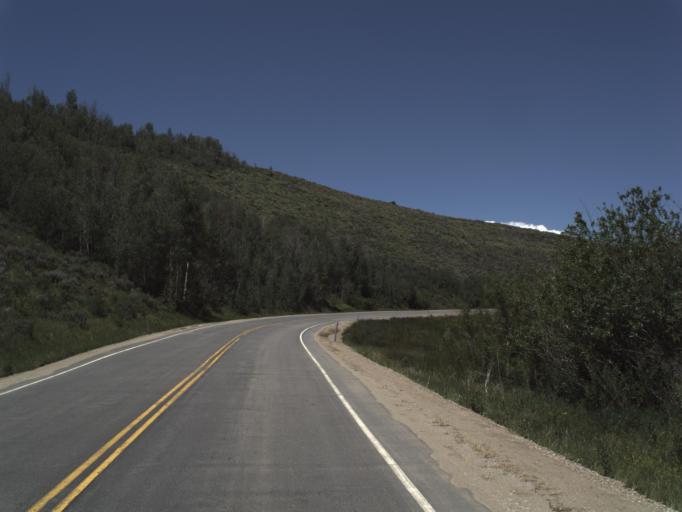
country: US
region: Utah
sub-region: Weber County
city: Wolf Creek
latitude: 41.4009
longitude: -111.5991
